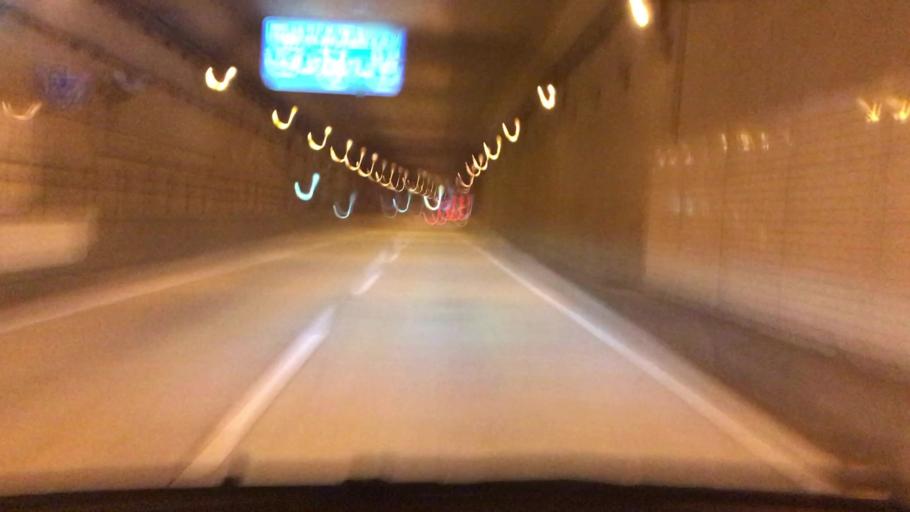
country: JP
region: Hyogo
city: Kobe
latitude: 34.7248
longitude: 135.1839
